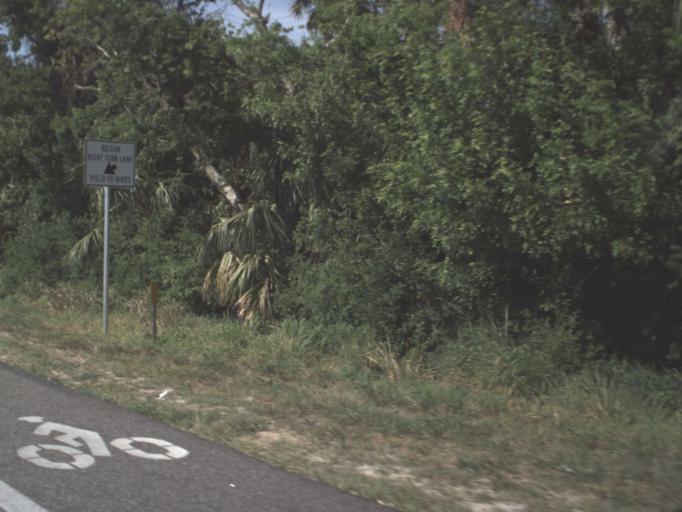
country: US
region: Florida
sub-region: Brevard County
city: Sharpes
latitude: 28.4308
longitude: -80.7595
